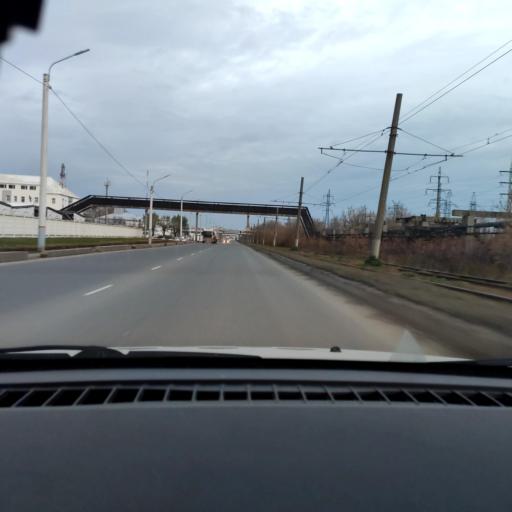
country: RU
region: Perm
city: Gamovo
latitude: 57.9202
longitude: 56.1456
